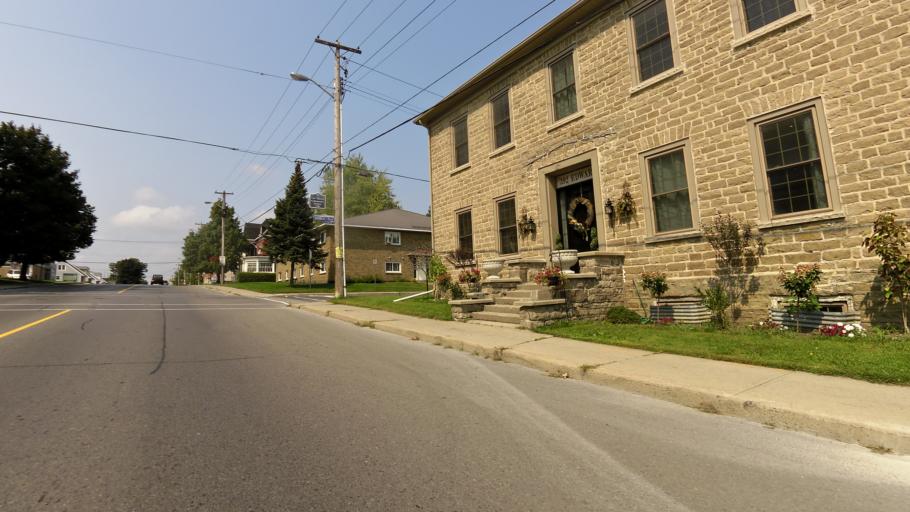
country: CA
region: Ontario
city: Prescott
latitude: 44.7116
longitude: -75.5142
